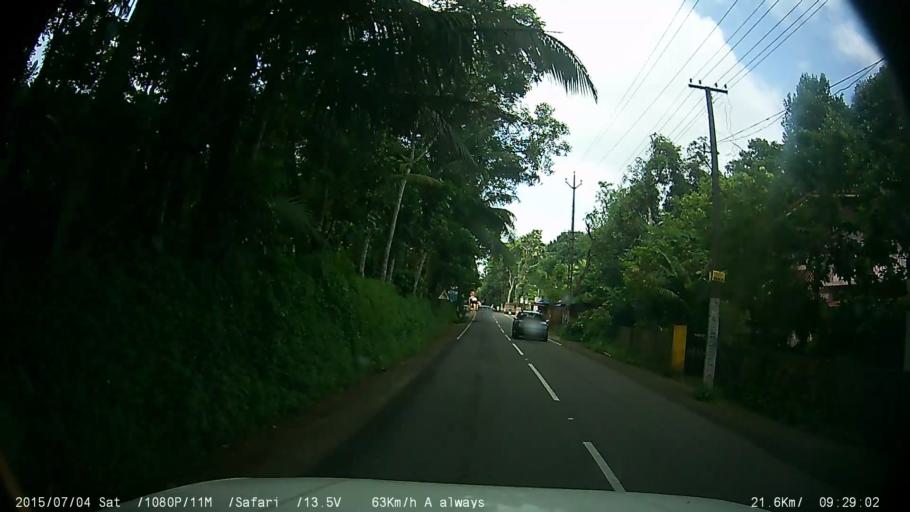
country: IN
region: Kerala
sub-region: Kottayam
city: Kottayam
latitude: 9.6408
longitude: 76.6070
